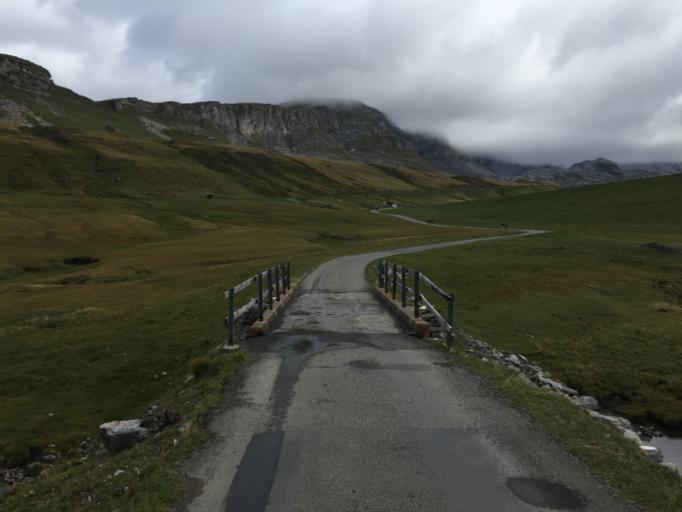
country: CH
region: Obwalden
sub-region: Obwalden
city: Engelberg
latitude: 46.7732
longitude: 8.2989
